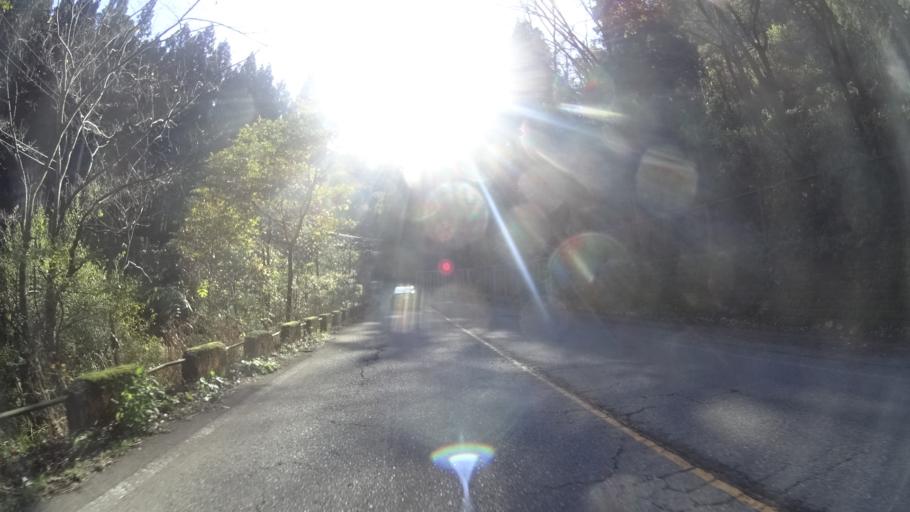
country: JP
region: Ishikawa
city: Tsurugi-asahimachi
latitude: 36.3729
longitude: 136.5767
